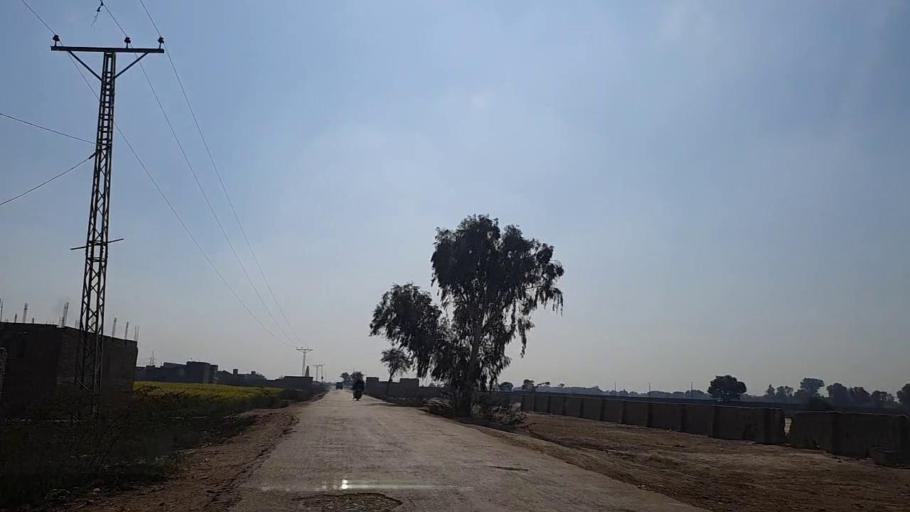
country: PK
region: Sindh
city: Sakrand
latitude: 26.2955
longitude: 68.1081
